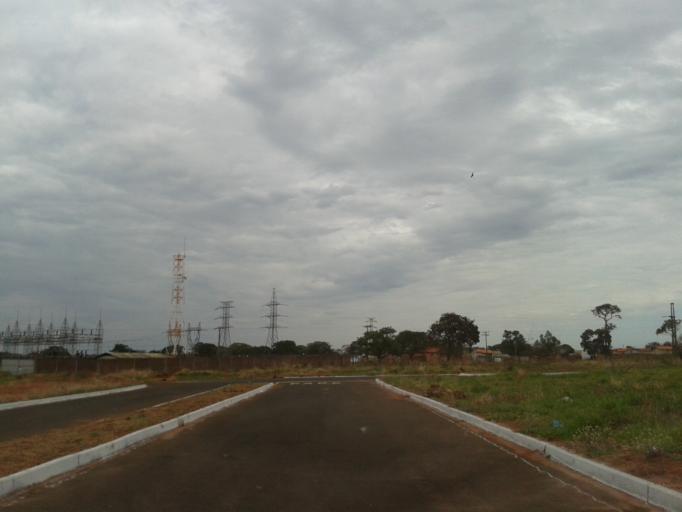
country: BR
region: Minas Gerais
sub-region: Santa Vitoria
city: Santa Vitoria
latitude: -18.8536
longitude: -50.1224
